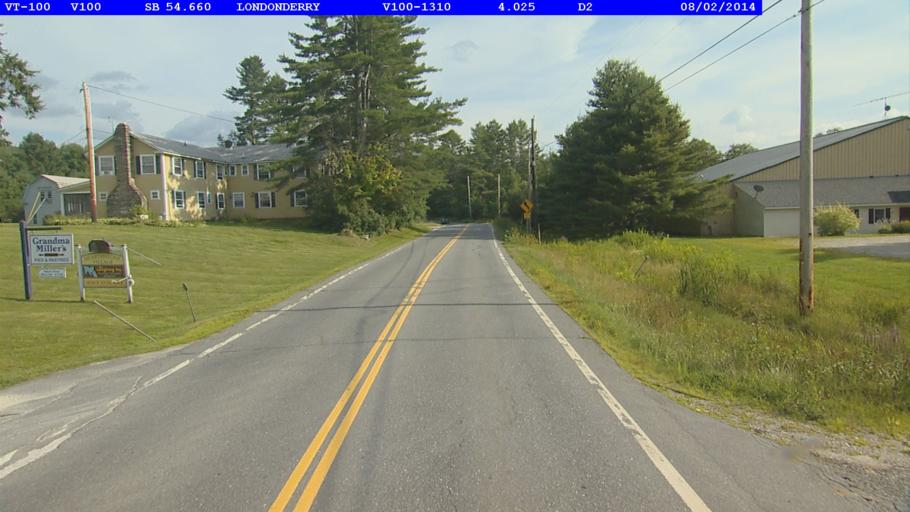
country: US
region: Vermont
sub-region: Windsor County
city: Chester
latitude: 43.2054
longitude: -72.8228
